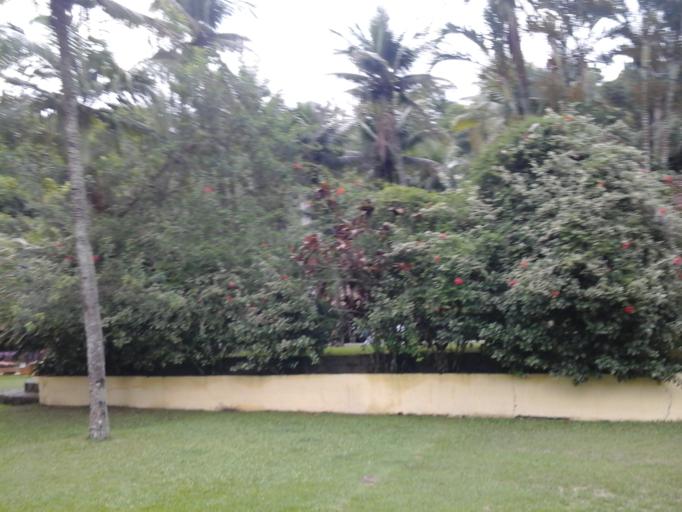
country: BR
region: Rio de Janeiro
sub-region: Nilopolis
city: Nilopolis
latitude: -22.9779
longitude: -43.4539
